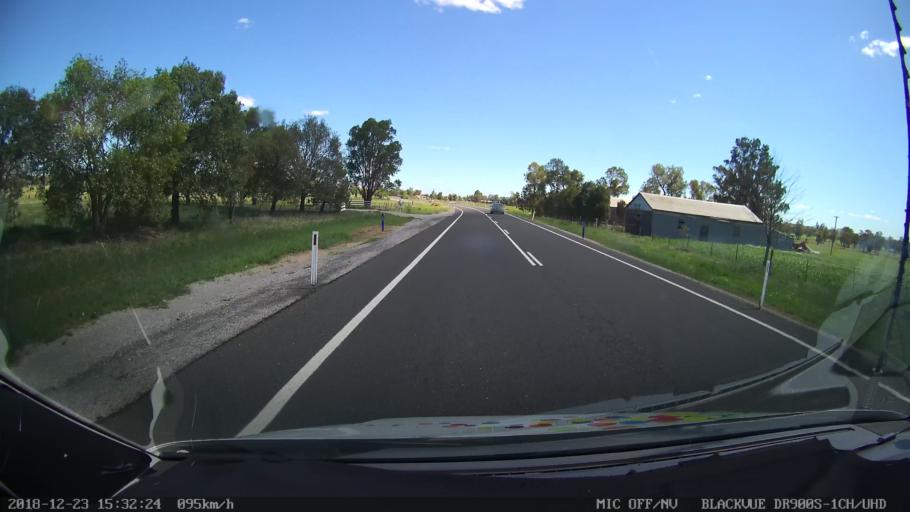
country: AU
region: New South Wales
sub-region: Tamworth Municipality
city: East Tamworth
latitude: -30.9852
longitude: 150.8701
